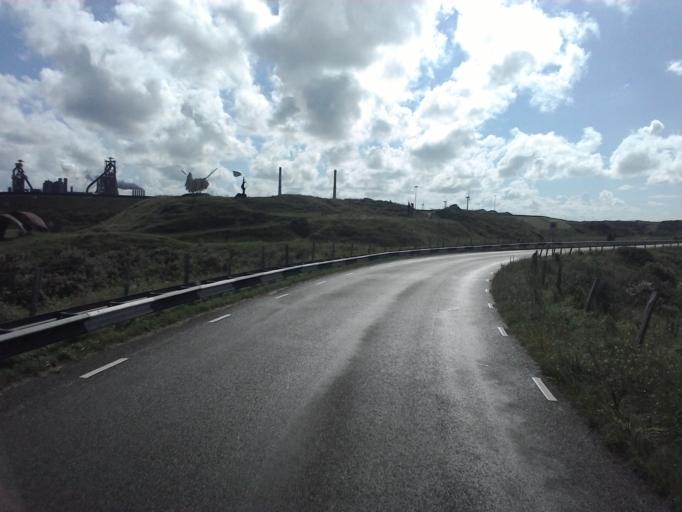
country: NL
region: North Holland
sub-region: Gemeente Velsen
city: Velsen-Zuid
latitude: 52.4886
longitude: 4.5913
